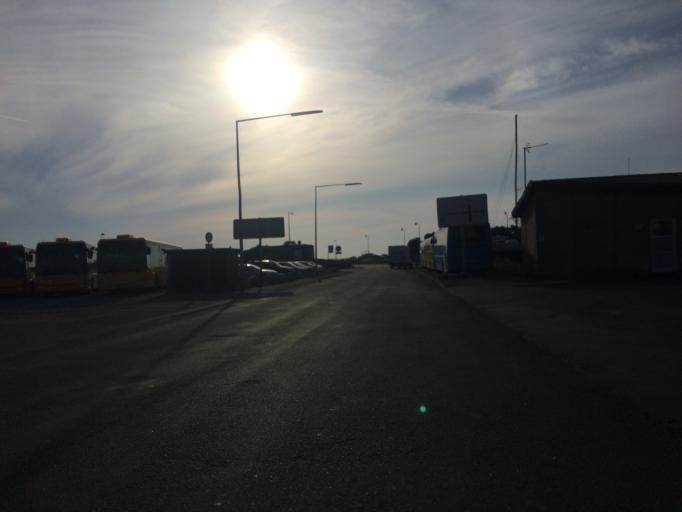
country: DK
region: Capital Region
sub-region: Bornholm Kommune
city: Ronne
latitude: 55.1026
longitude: 14.6926
